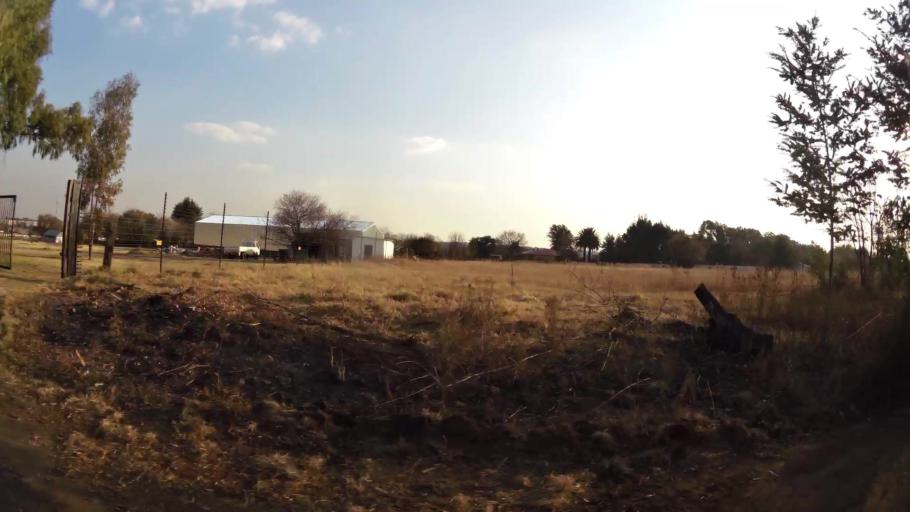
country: ZA
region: Gauteng
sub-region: Ekurhuleni Metropolitan Municipality
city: Benoni
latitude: -26.1548
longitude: 28.3682
